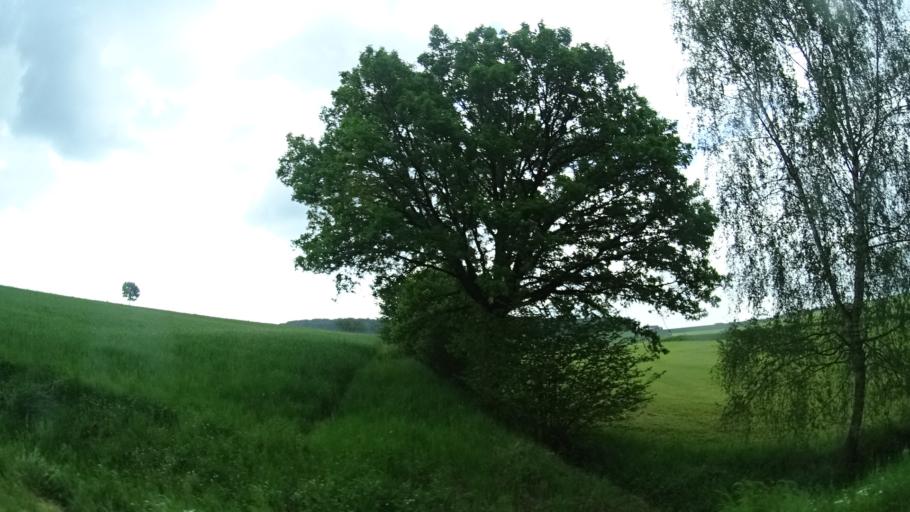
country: DE
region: Bavaria
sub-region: Regierungsbezirk Unterfranken
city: Wartmannsroth
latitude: 50.1413
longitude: 9.7730
